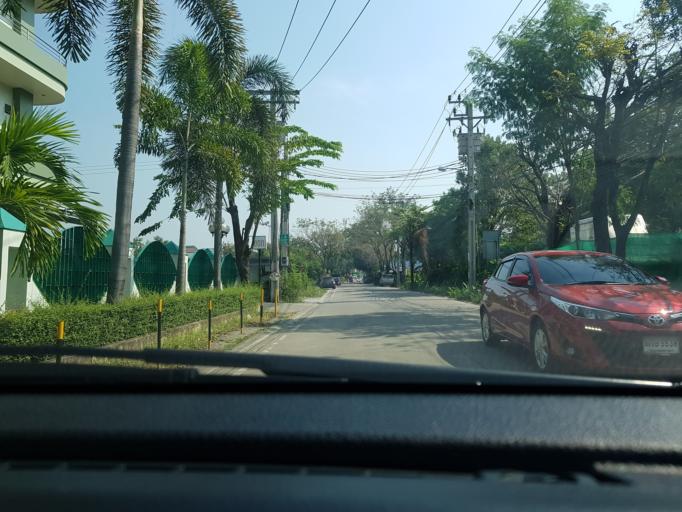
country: TH
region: Bangkok
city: Phasi Charoen
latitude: 13.7301
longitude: 100.4536
